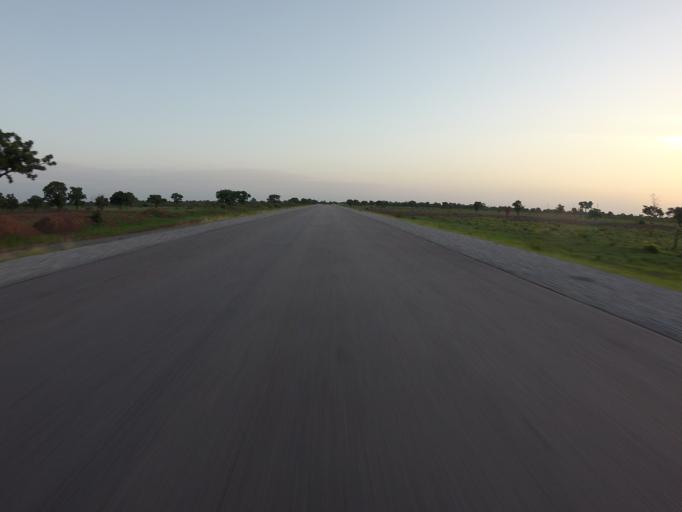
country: GH
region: Northern
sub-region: Yendi
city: Yendi
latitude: 9.9520
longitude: -0.1546
